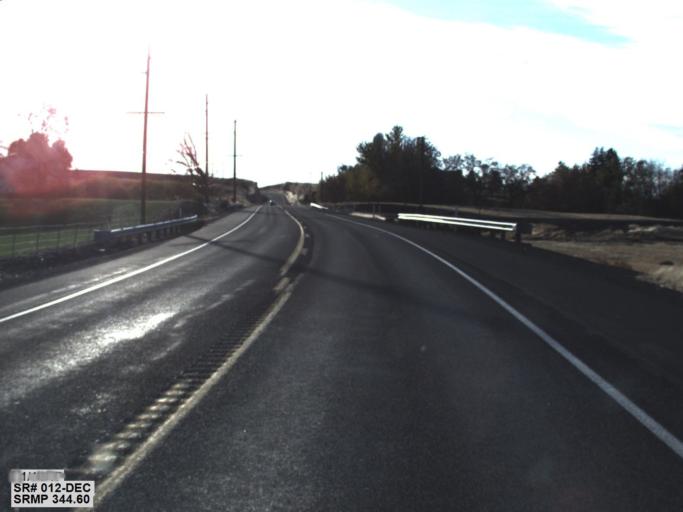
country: US
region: Washington
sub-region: Walla Walla County
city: Walla Walla East
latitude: 46.1193
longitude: -118.2143
